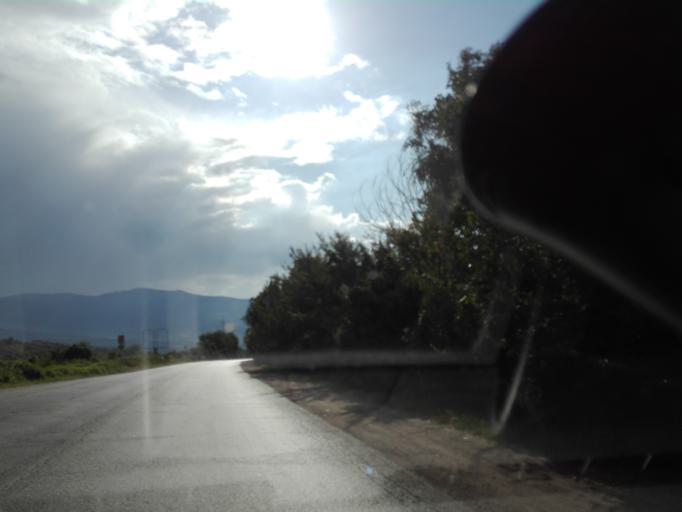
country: BG
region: Sofia-Capital
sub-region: Stolichna Obshtina
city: Sofia
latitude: 42.6220
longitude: 23.4393
